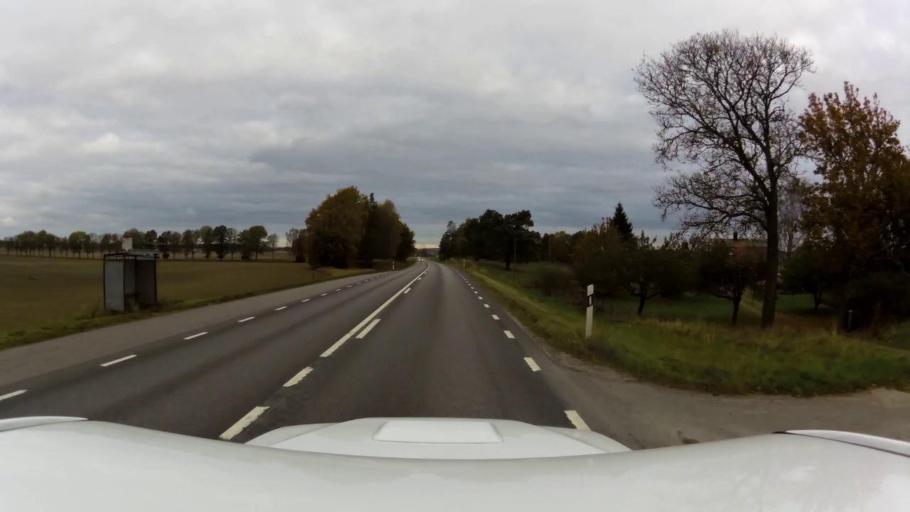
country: SE
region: OEstergoetland
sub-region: Linkopings Kommun
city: Ljungsbro
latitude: 58.5076
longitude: 15.4490
